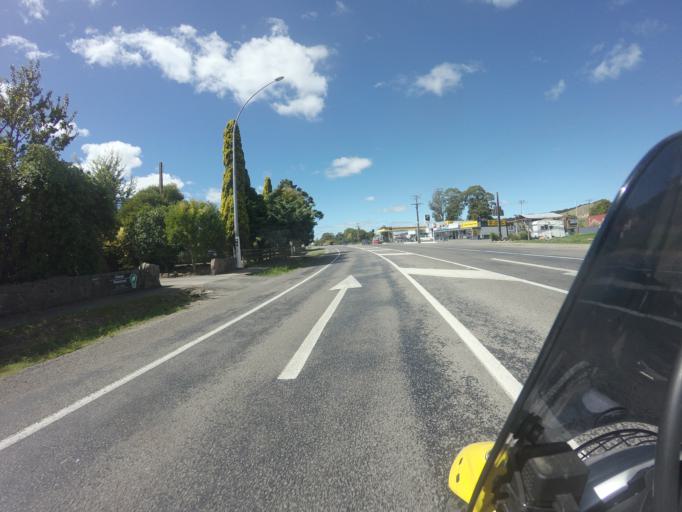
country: NZ
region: Bay of Plenty
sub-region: Whakatane District
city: Edgecumbe
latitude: -37.9985
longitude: 176.8900
